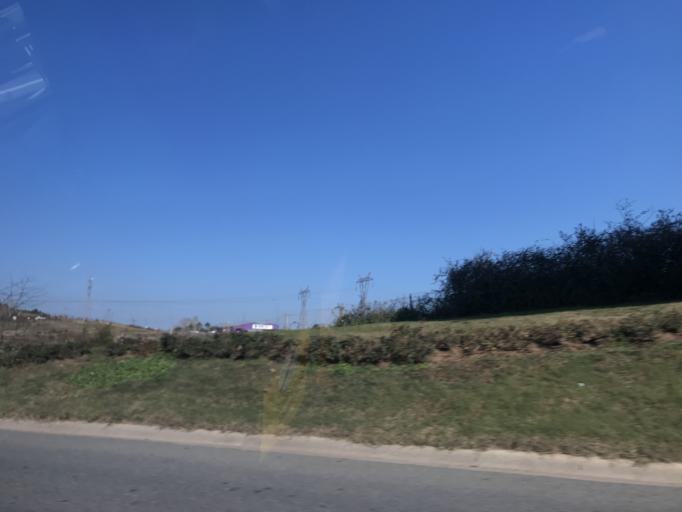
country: TR
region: Istanbul
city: Sultanbeyli
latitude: 40.9383
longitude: 29.3326
